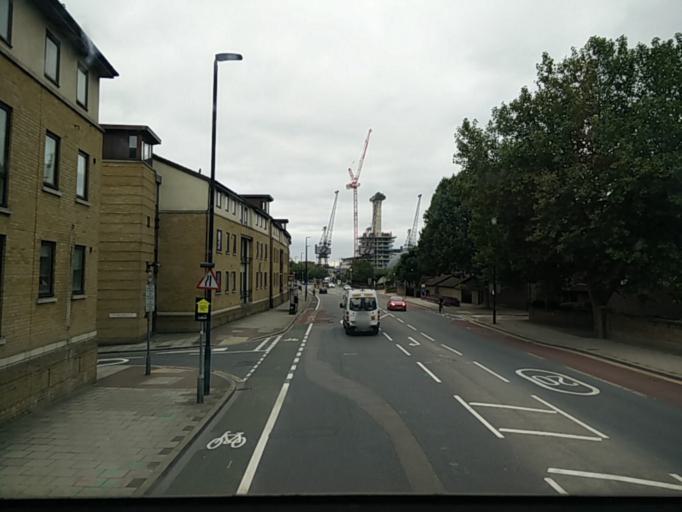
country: GB
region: England
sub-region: Greater London
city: Poplar
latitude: 51.5039
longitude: -0.0078
